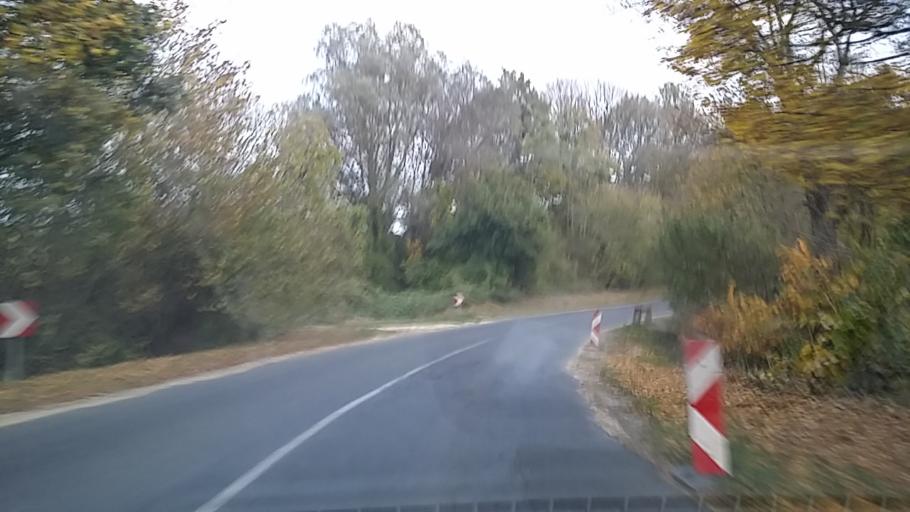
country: HU
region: Veszprem
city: Zirc
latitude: 47.2288
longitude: 17.8081
